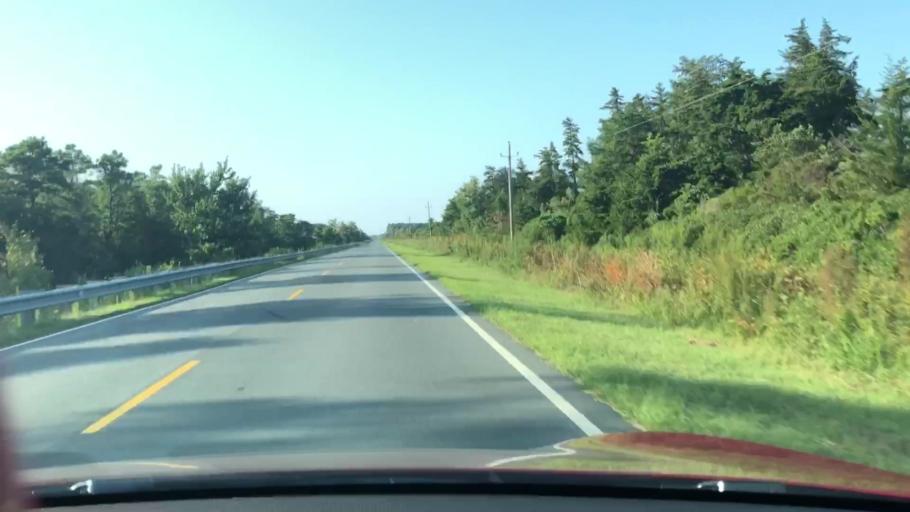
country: US
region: North Carolina
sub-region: Dare County
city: Wanchese
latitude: 35.7552
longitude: -75.7688
